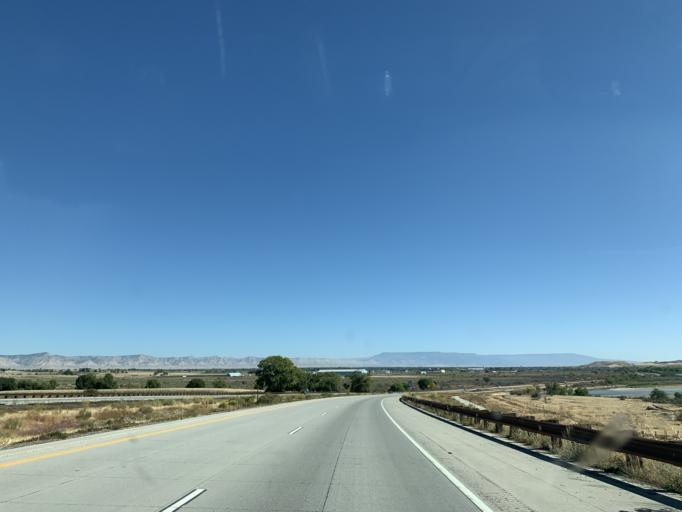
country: US
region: Colorado
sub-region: Mesa County
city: Loma
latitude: 39.1775
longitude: -108.8074
